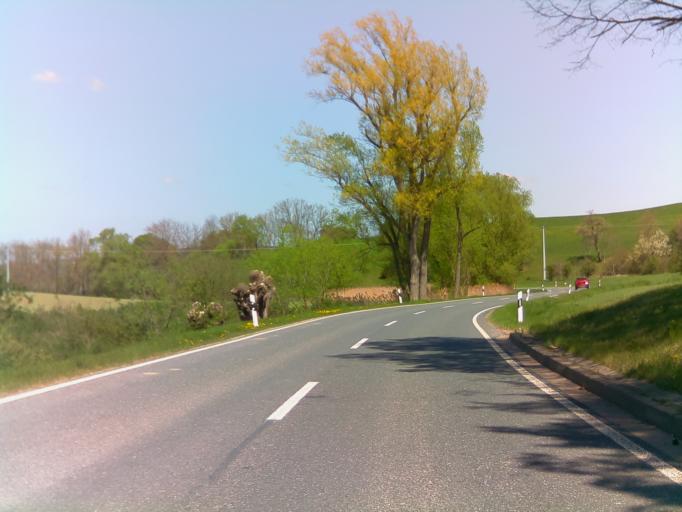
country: DE
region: Thuringia
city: Stadtilm
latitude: 50.7391
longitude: 11.0655
